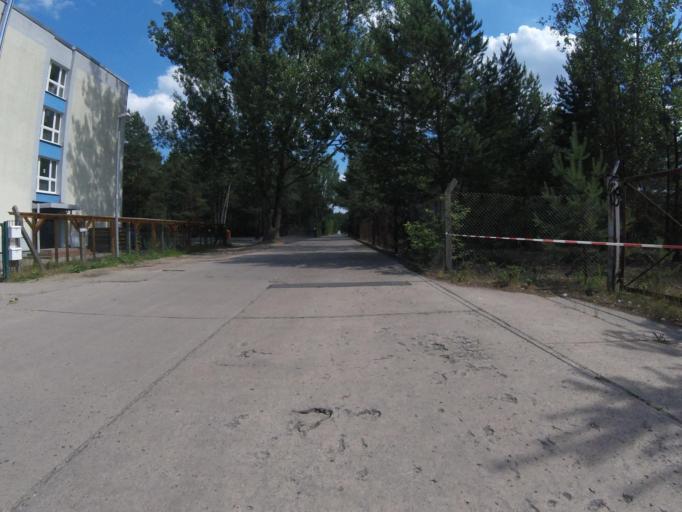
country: DE
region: Berlin
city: Schmockwitz
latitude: 52.3406
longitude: 13.6687
